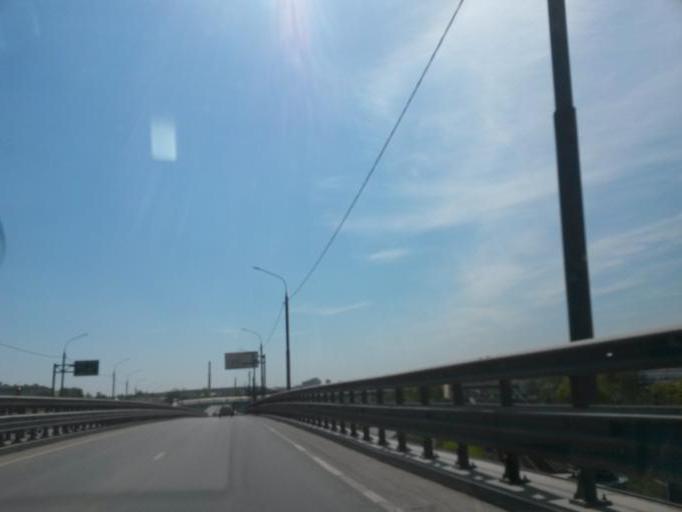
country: RU
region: Moskovskaya
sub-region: Podol'skiy Rayon
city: Podol'sk
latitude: 55.4072
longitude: 37.5515
